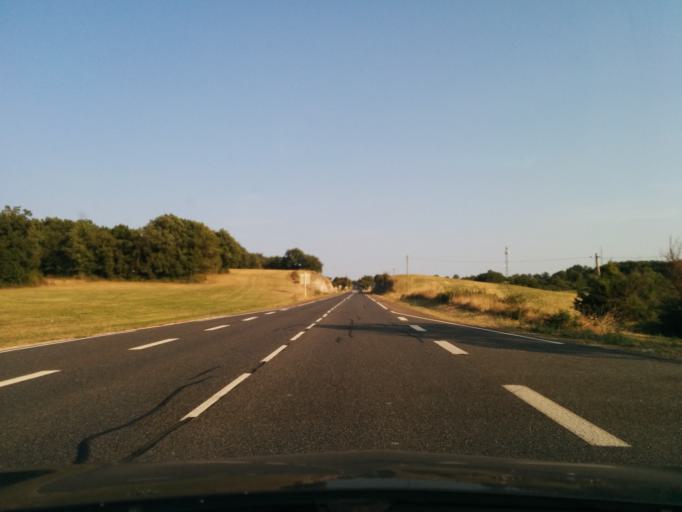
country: FR
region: Midi-Pyrenees
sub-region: Departement du Lot
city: Le Vigan
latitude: 44.6212
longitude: 1.4903
